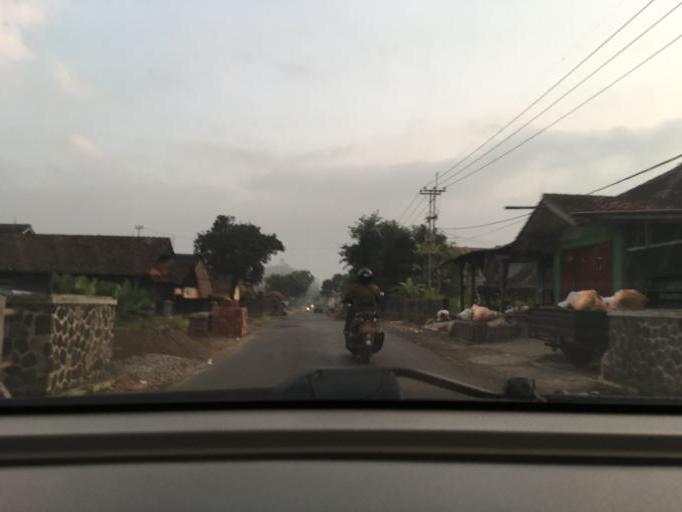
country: ID
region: West Java
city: Pasireurih
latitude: -7.1845
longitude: 108.1970
